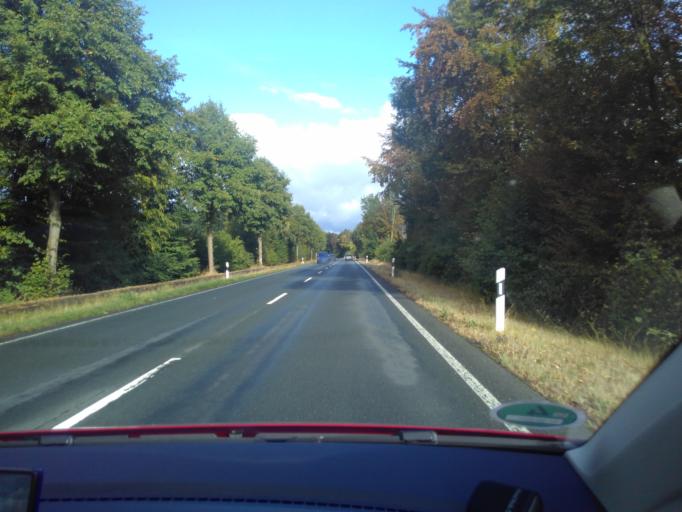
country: DE
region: North Rhine-Westphalia
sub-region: Regierungsbezirk Munster
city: Ostbevern
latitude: 52.0104
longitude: 7.9219
